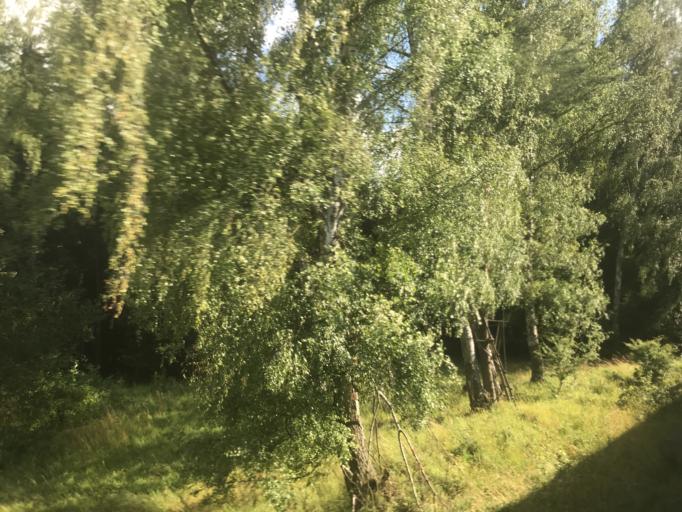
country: CZ
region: Jihocesky
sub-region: Okres Cesky Krumlov
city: Dolni Dvoriste
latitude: 48.6730
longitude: 14.4433
